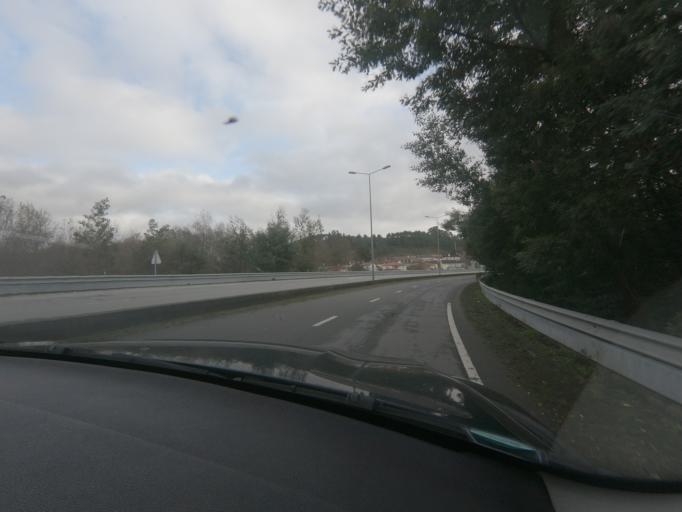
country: PT
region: Viseu
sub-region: Viseu
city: Campo
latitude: 40.7016
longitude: -7.9337
